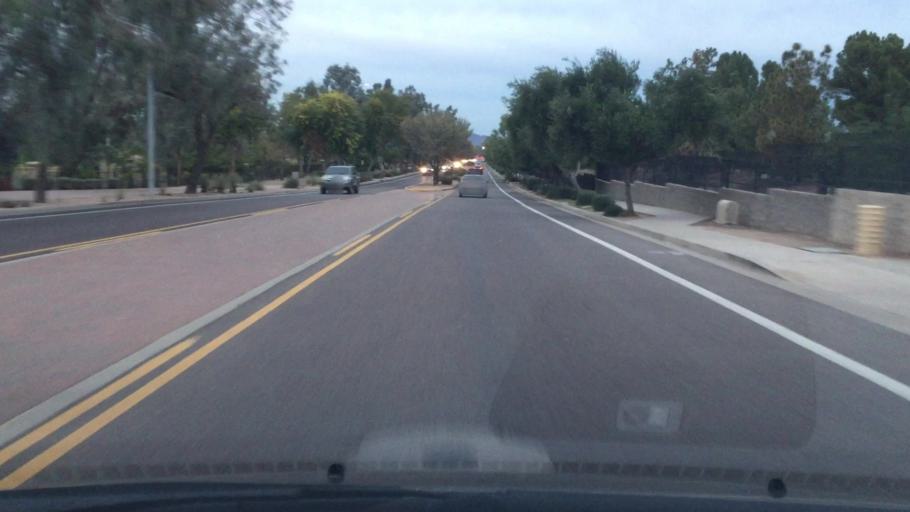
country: US
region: Arizona
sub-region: Maricopa County
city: Guadalupe
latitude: 33.3797
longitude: -112.0127
